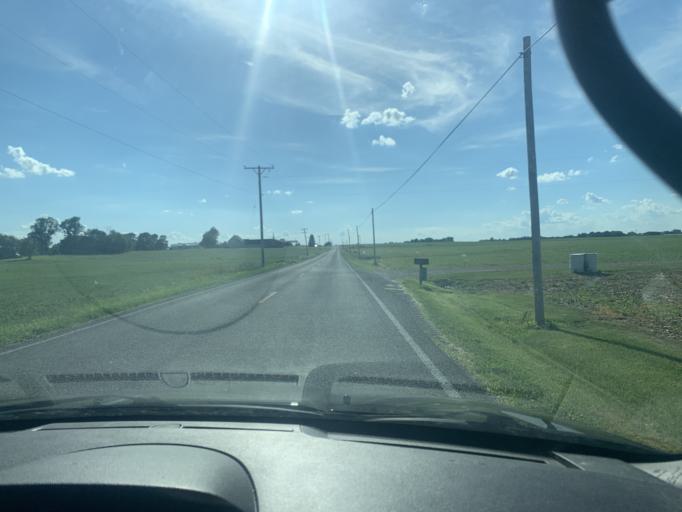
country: US
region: Ohio
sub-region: Logan County
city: Bellefontaine
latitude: 40.3441
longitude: -83.8378
